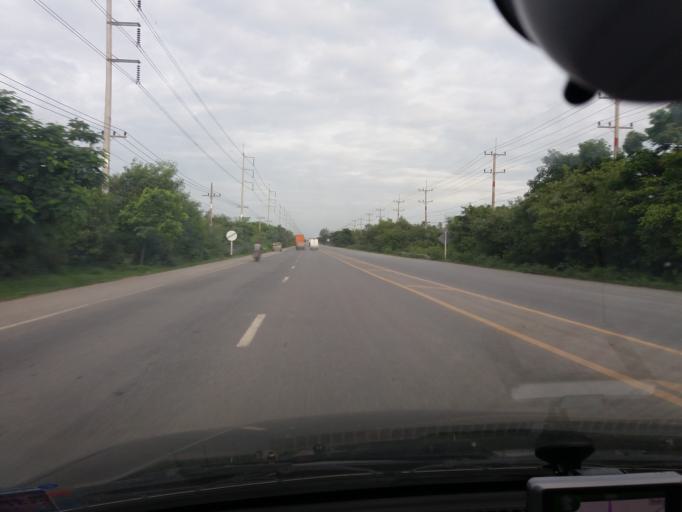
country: TH
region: Suphan Buri
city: U Thong
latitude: 14.3375
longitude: 99.8381
